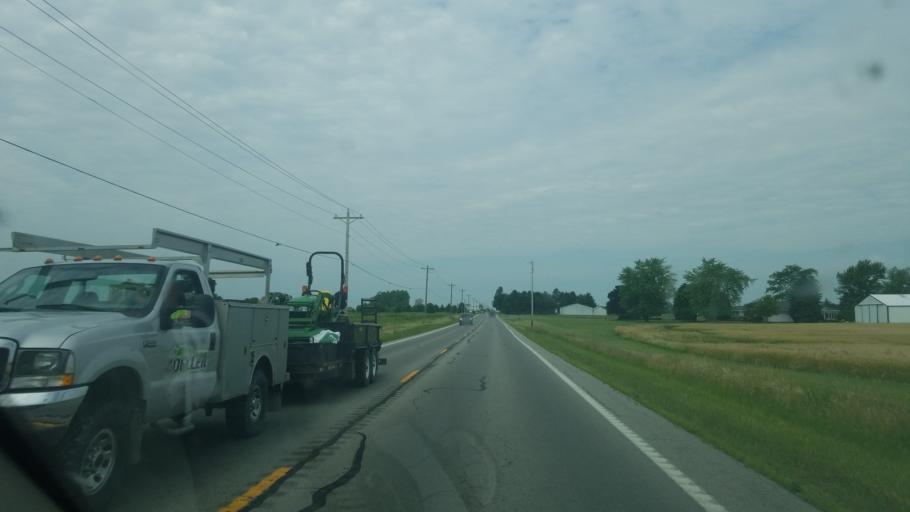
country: US
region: Ohio
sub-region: Seneca County
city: Fostoria
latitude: 41.0728
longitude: -83.4652
